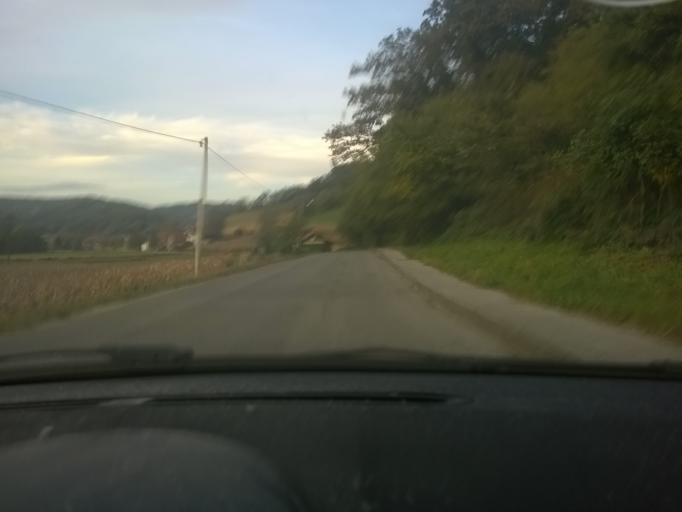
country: HR
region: Krapinsko-Zagorska
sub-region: Grad Krapina
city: Krapina
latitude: 46.1412
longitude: 15.8508
